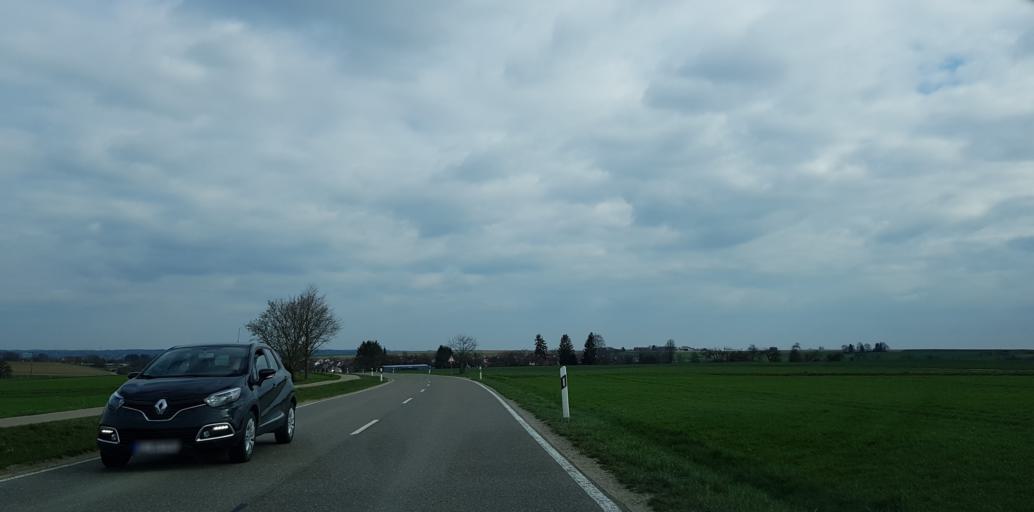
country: DE
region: Baden-Wuerttemberg
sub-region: Tuebingen Region
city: Erbach
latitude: 48.3595
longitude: 9.8883
